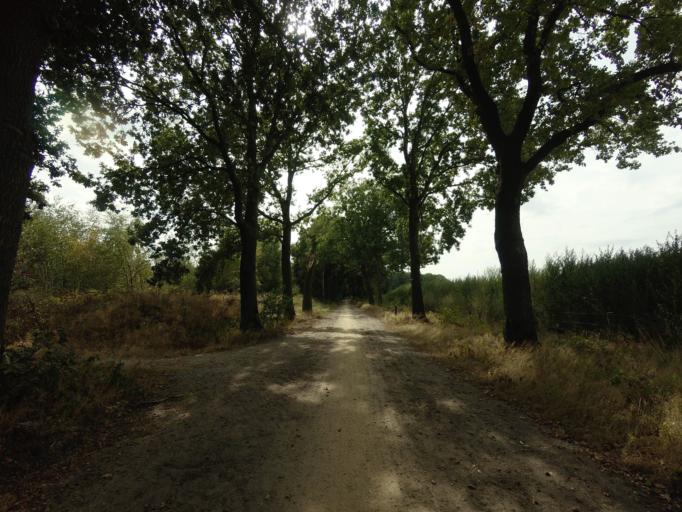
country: NL
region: North Brabant
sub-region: Gemeente Helmond
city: Helmond
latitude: 51.5194
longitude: 5.7616
